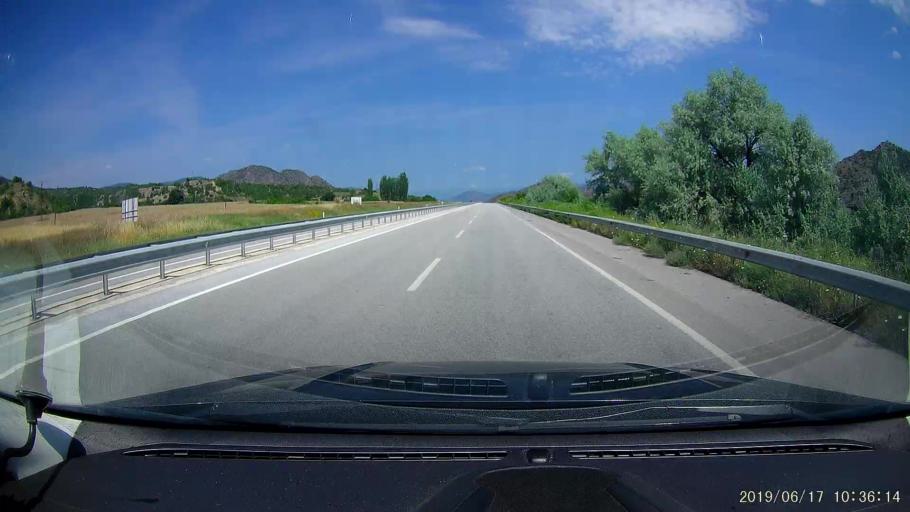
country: TR
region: Corum
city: Osmancik
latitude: 40.9765
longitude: 34.6853
